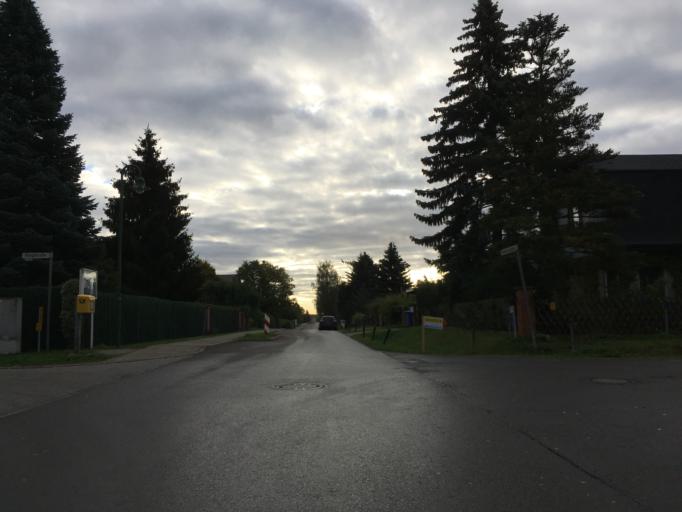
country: DE
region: Berlin
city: Wartenberg
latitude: 52.5913
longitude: 13.5347
